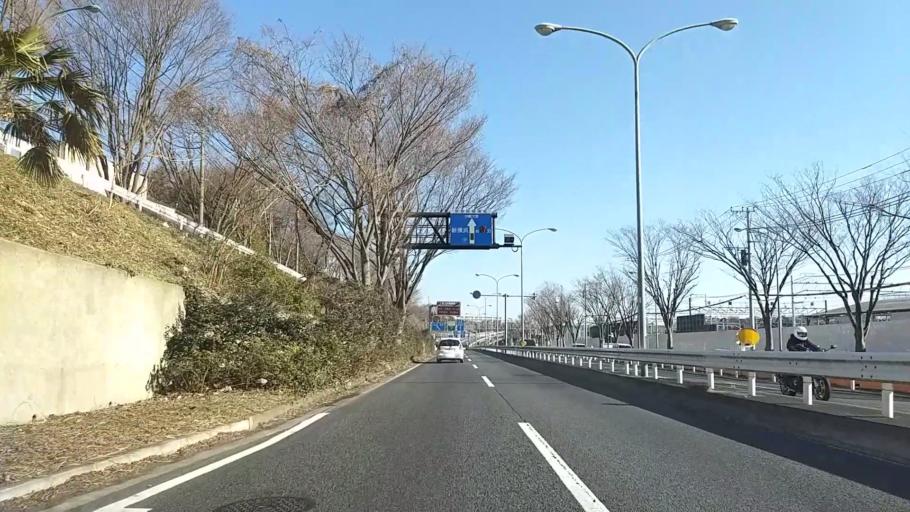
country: JP
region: Kanagawa
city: Yokohama
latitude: 35.4825
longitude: 139.5871
